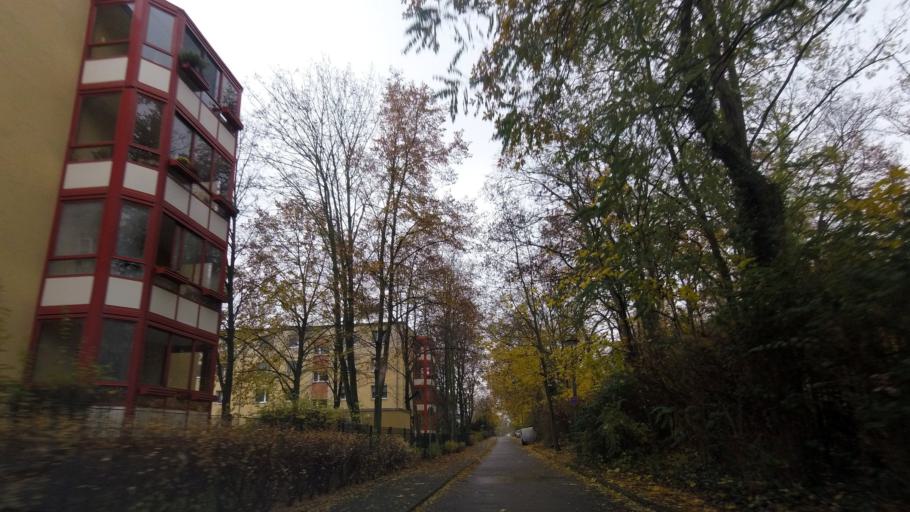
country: DE
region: Berlin
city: Weissensee
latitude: 52.5604
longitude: 13.4528
